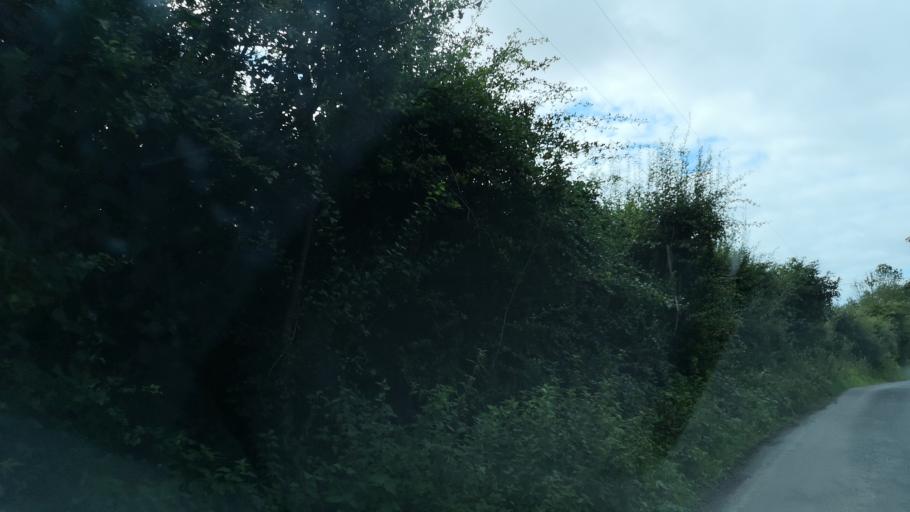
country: IE
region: Connaught
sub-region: County Galway
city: Moycullen
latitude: 53.3200
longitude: -9.1419
